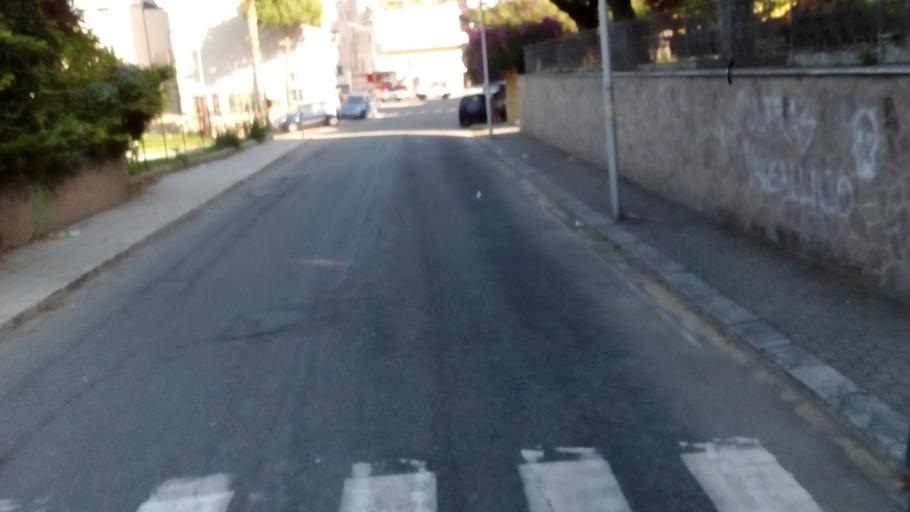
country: IT
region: Calabria
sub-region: Provincia di Reggio Calabria
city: Campo Calabro
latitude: 38.2115
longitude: 15.6368
